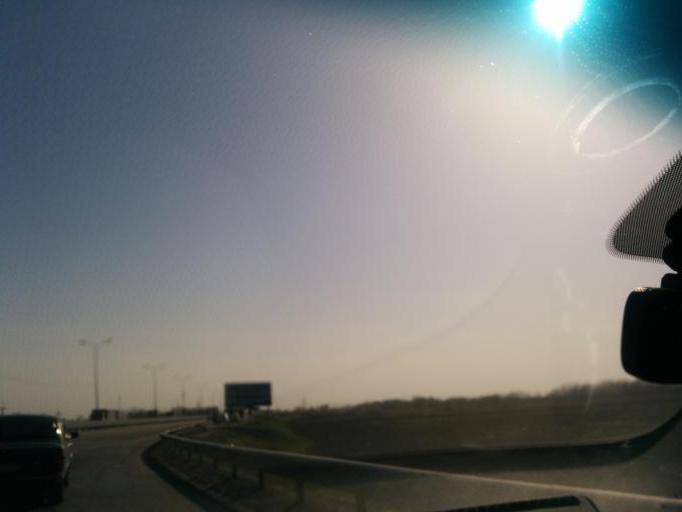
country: RU
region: Rostov
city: Mayskiy
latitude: 47.7109
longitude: 40.1003
